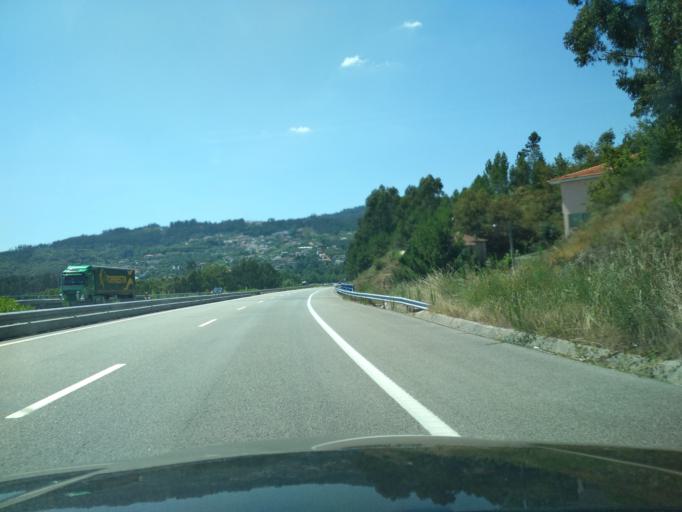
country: PT
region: Braga
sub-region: Guimaraes
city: Serzedo
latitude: 41.4072
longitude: -8.2117
